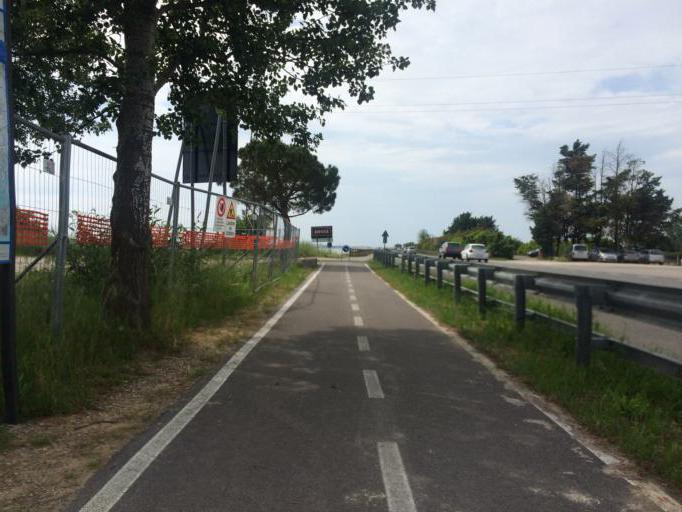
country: IT
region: Friuli Venezia Giulia
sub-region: Provincia di Udine
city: Aquileia
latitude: 45.7254
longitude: 13.3864
